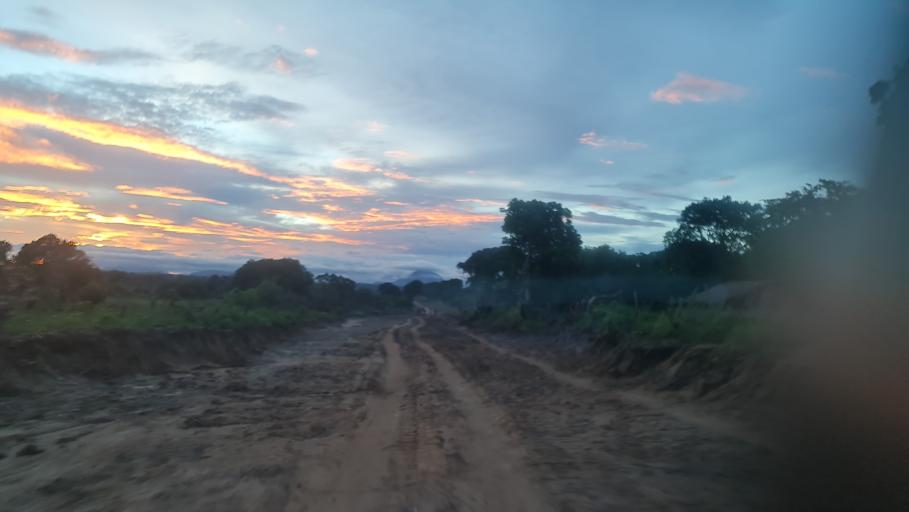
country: MZ
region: Nampula
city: Nampula
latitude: -14.7336
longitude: 39.9162
